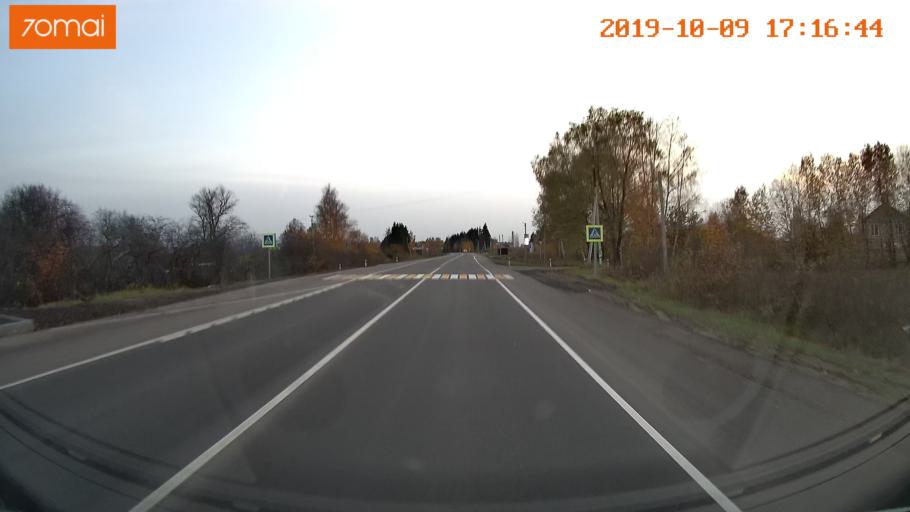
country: RU
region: Ivanovo
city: Furmanov
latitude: 57.2849
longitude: 41.1617
